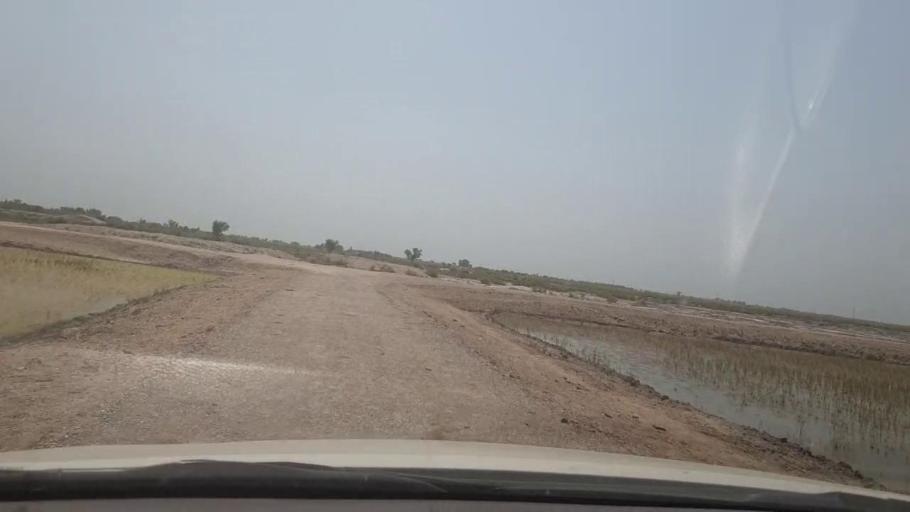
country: PK
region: Sindh
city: Shikarpur
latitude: 28.0268
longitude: 68.5685
